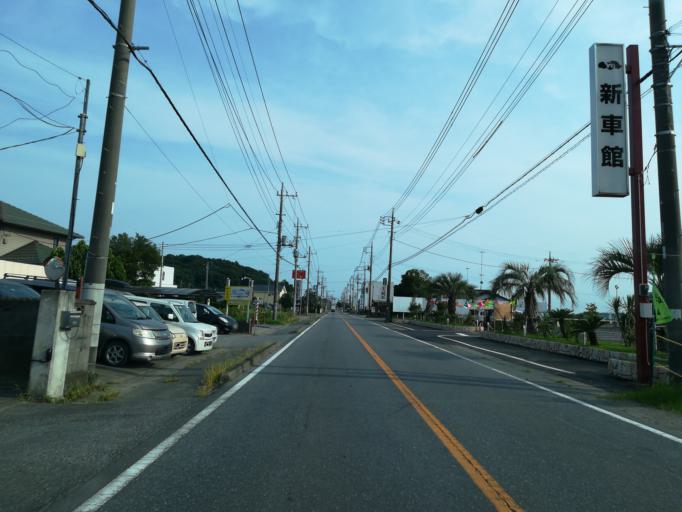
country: JP
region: Ibaraki
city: Tsukuba
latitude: 36.1935
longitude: 140.0788
